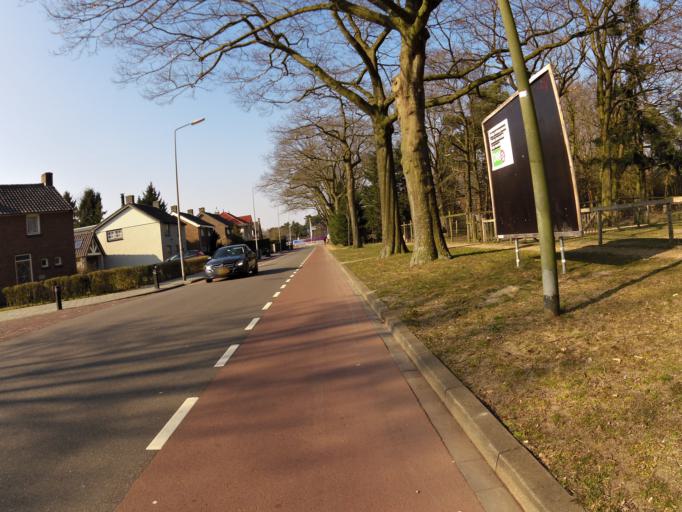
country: NL
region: North Brabant
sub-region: Gemeente Sint-Michielsgestel
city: Sint-Michielsgestel
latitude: 51.7075
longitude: 5.3825
